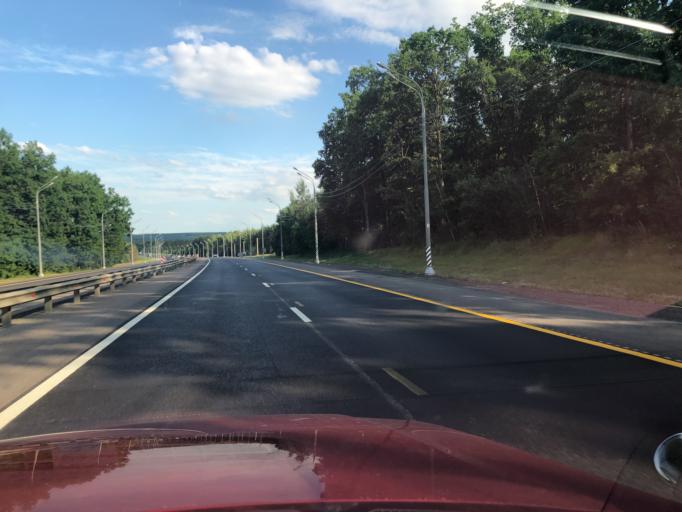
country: RU
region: Lipetsk
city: Zadonsk
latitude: 52.3841
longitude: 38.8705
